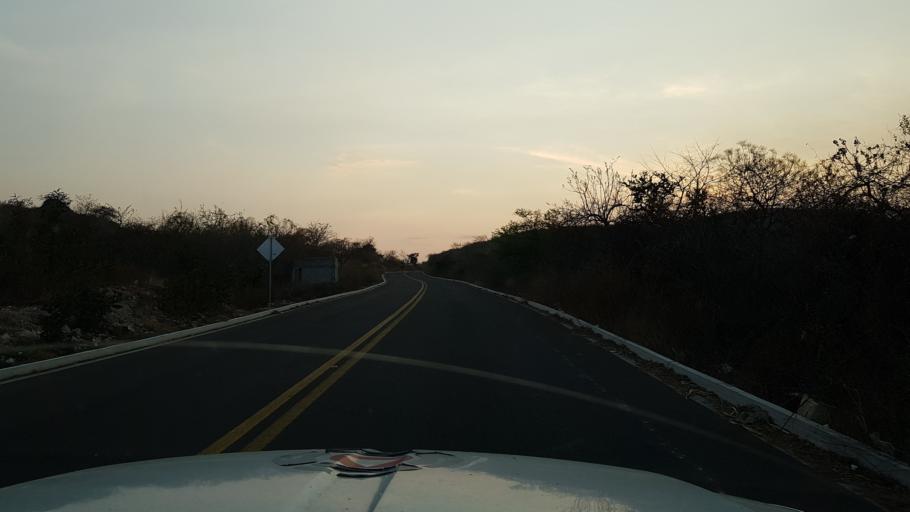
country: MX
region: Morelos
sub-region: Ayala
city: Olintepec
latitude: 18.7336
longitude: -99.0139
